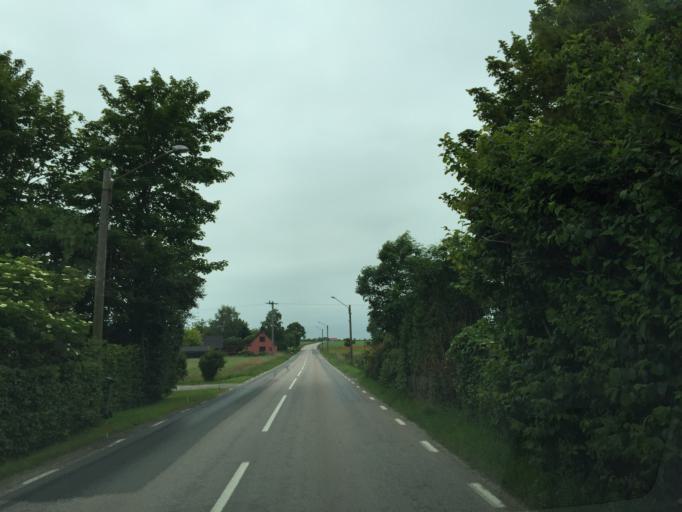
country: SE
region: Skane
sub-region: Ystads Kommun
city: Kopingebro
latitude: 55.4281
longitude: 14.0967
